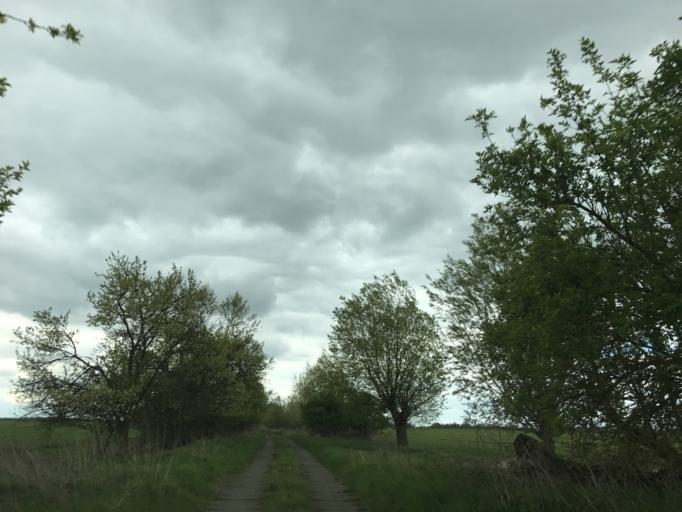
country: DE
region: Brandenburg
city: Roskow
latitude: 52.5061
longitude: 12.7791
